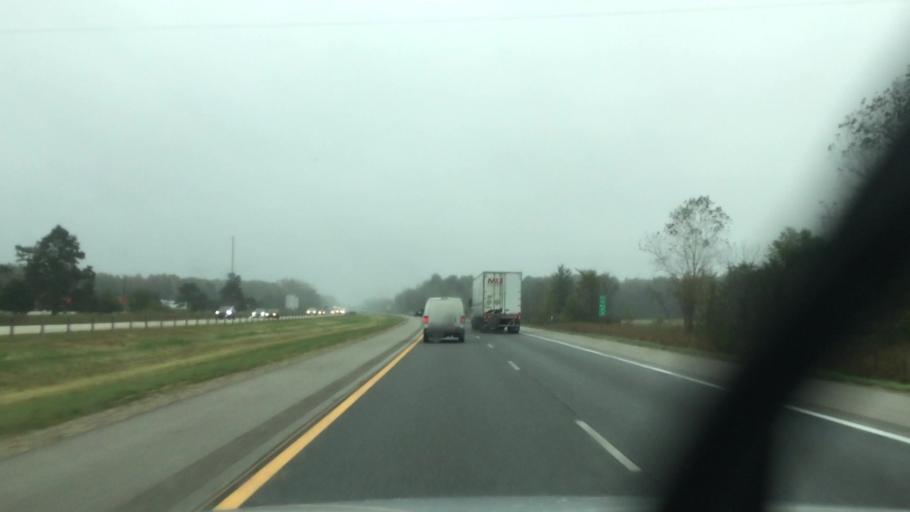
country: US
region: Michigan
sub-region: Berrien County
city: Watervliet
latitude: 42.1794
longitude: -86.2426
